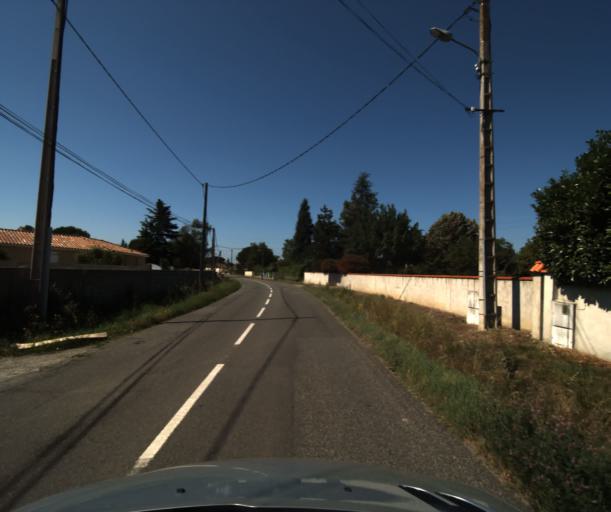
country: FR
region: Midi-Pyrenees
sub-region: Departement de la Haute-Garonne
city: Saubens
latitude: 43.4915
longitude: 1.3525
